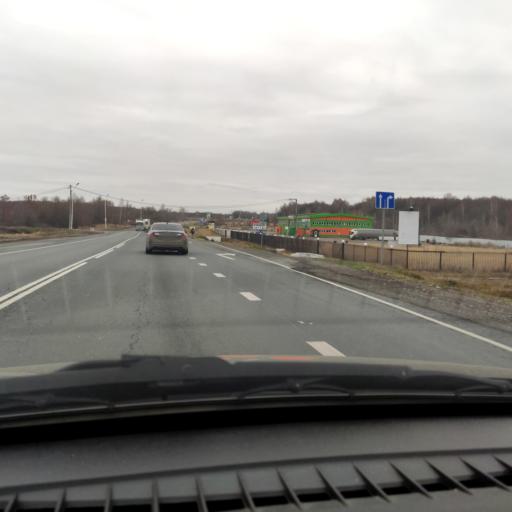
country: RU
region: Samara
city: Zhigulevsk
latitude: 53.3463
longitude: 49.4502
